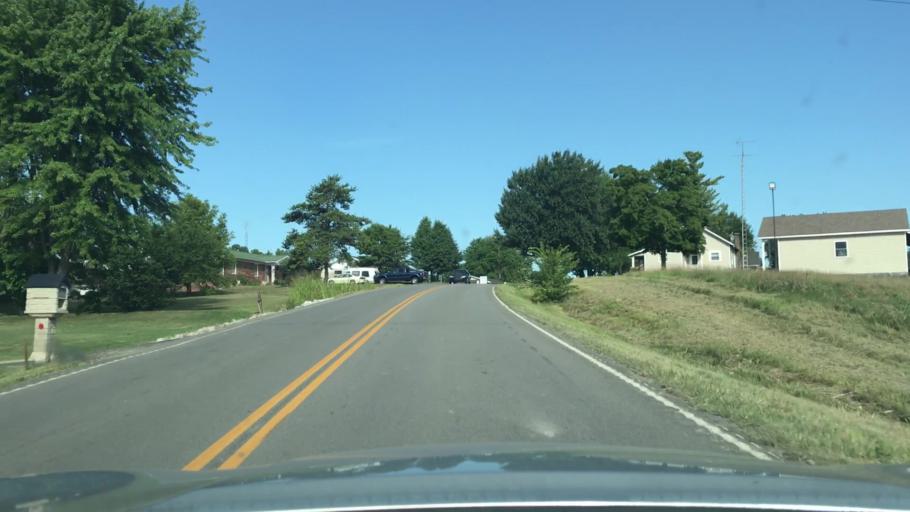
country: US
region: Kentucky
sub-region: Muhlenberg County
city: Greenville
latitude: 37.1869
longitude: -87.1648
